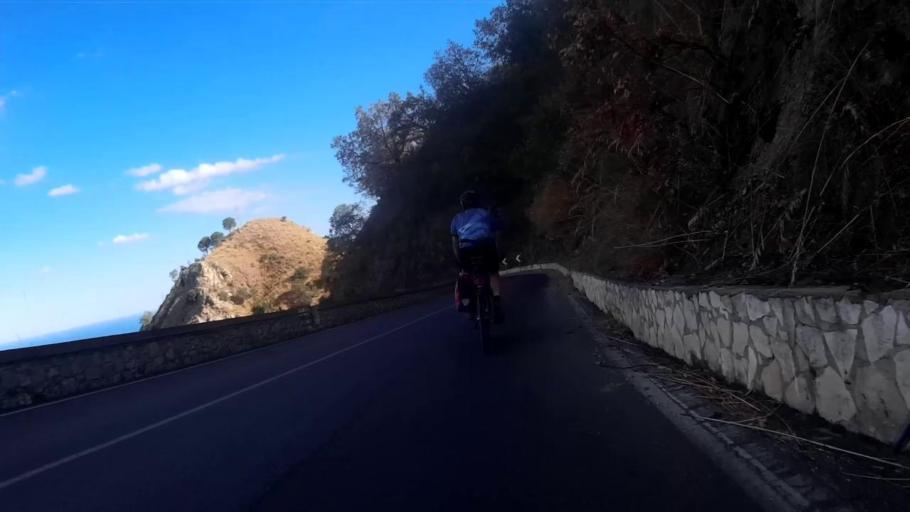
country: IT
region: Sicily
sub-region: Messina
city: Castelmola
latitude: 37.8625
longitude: 15.2786
